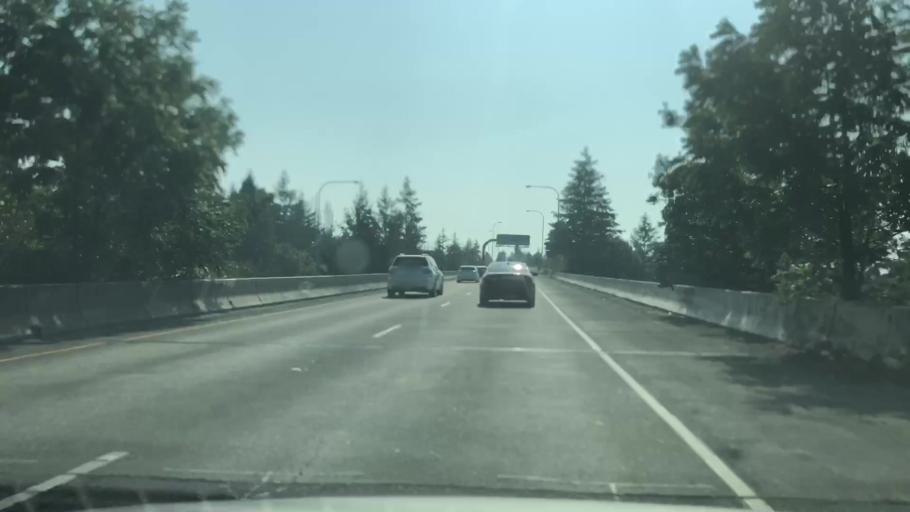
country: US
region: Washington
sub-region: Clark County
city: Minnehaha
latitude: 45.6508
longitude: -122.6561
